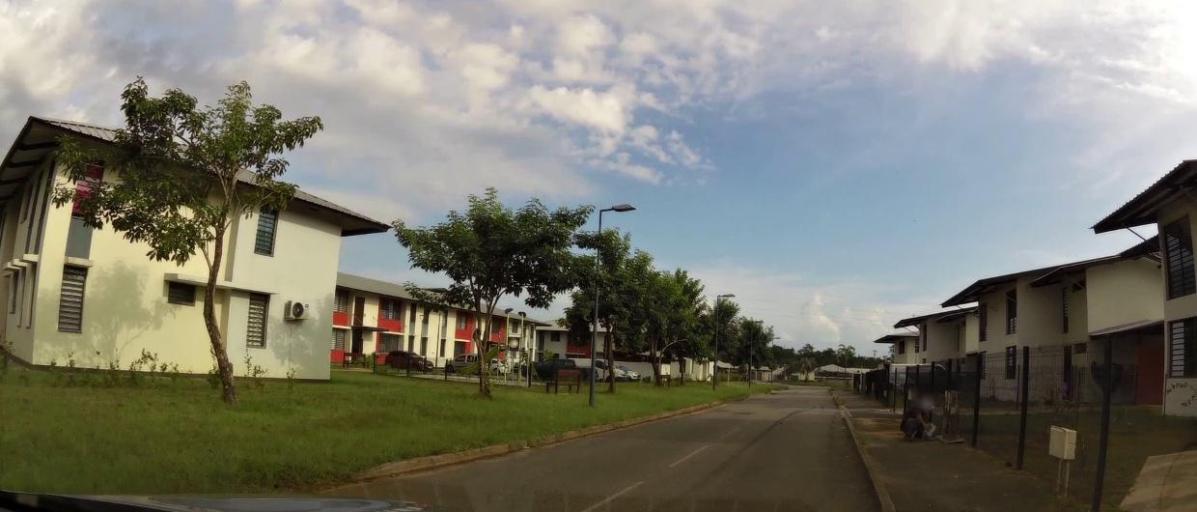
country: GF
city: Macouria
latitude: 4.9225
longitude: -52.4179
